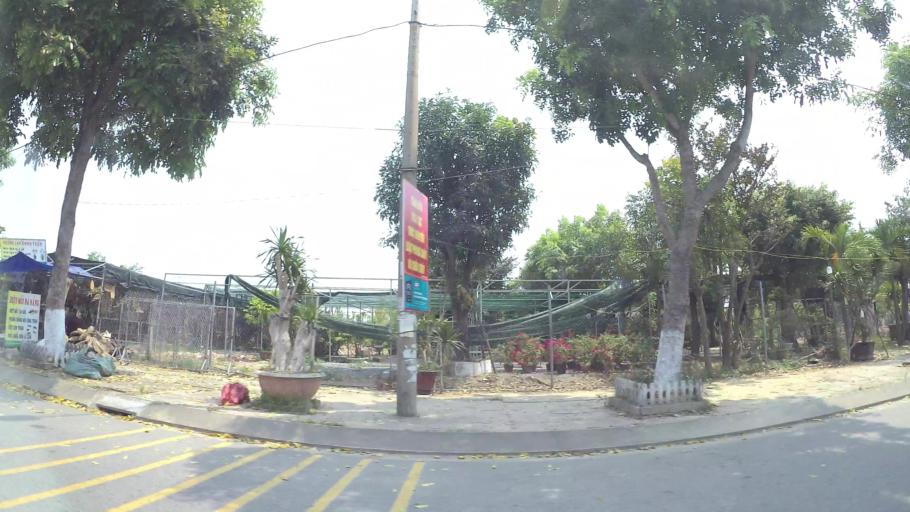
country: VN
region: Da Nang
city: Cam Le
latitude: 15.9948
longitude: 108.2074
